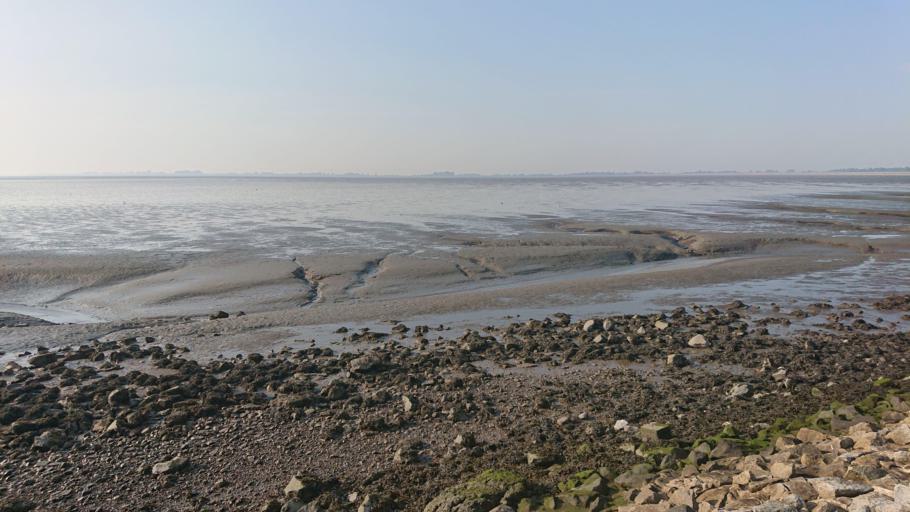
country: DE
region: Schleswig-Holstein
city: Wesselburenerkoog
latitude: 54.2667
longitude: 8.8412
